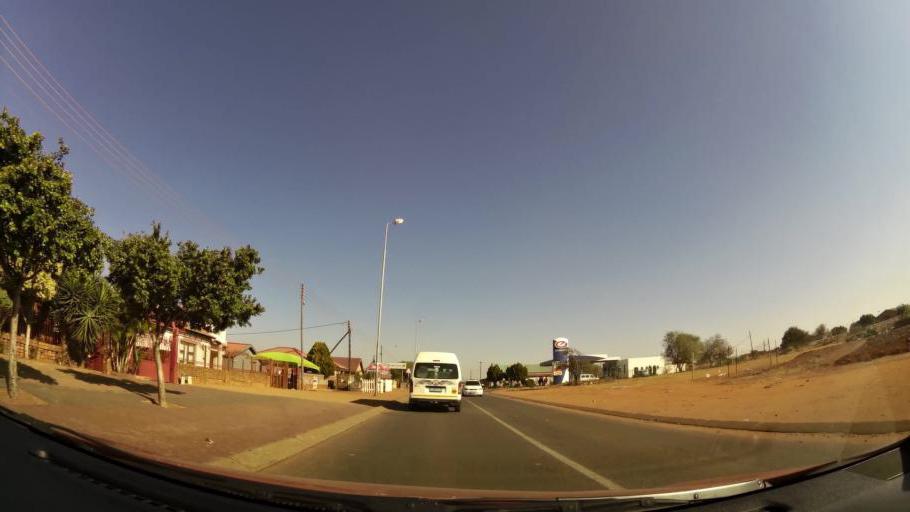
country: ZA
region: Gauteng
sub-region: City of Tshwane Metropolitan Municipality
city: Mabopane
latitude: -25.5400
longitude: 28.1052
